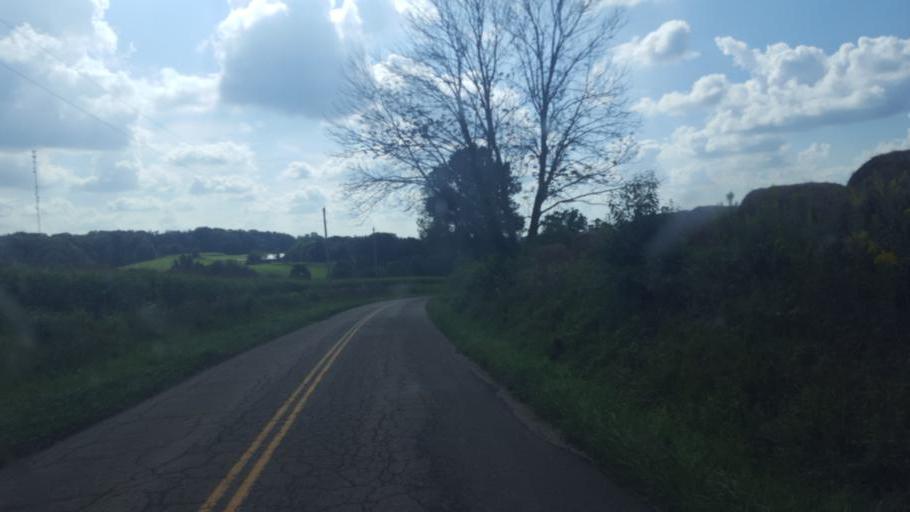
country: US
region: Ohio
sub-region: Knox County
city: Oak Hill
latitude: 40.4057
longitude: -82.2549
